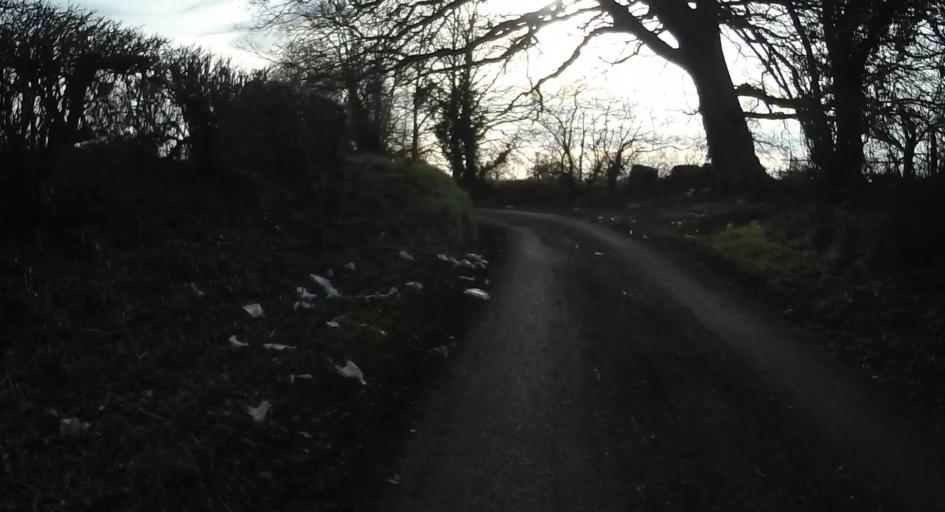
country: GB
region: England
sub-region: Wokingham
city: Swallowfield
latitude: 51.4106
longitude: -0.9971
